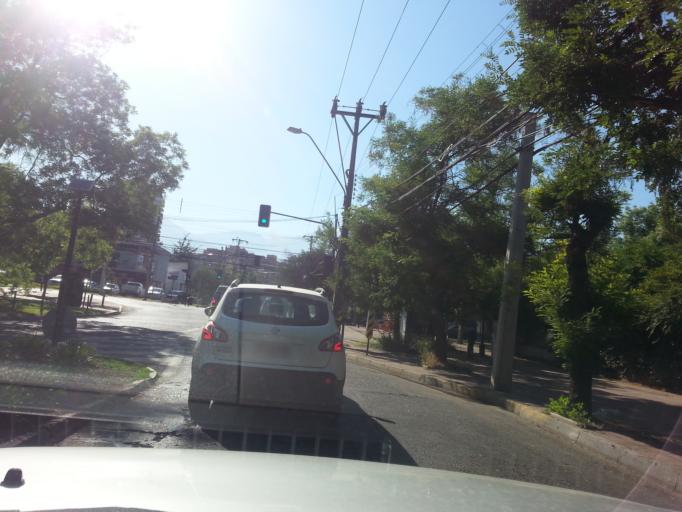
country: CL
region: Santiago Metropolitan
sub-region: Provincia de Santiago
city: Villa Presidente Frei, Nunoa, Santiago, Chile
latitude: -33.3926
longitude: -70.5816
